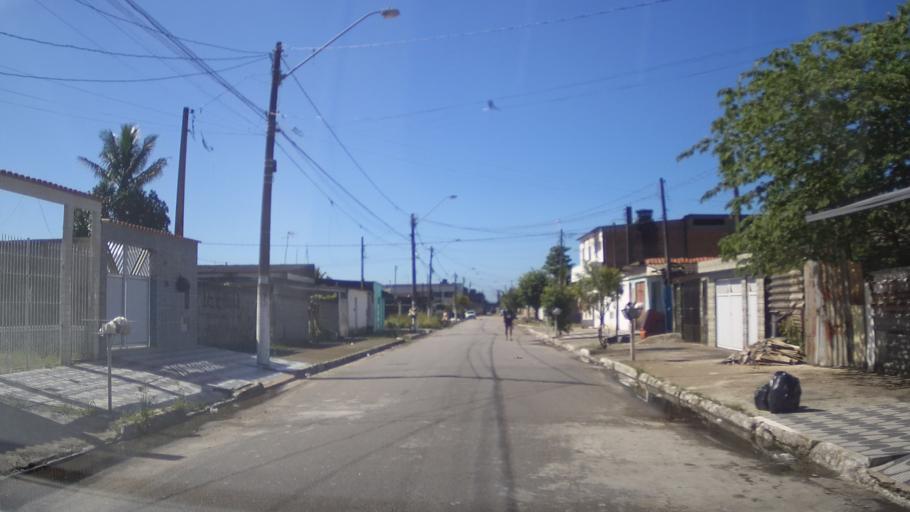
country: BR
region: Sao Paulo
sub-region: Mongagua
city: Mongagua
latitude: -24.0274
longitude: -46.5280
